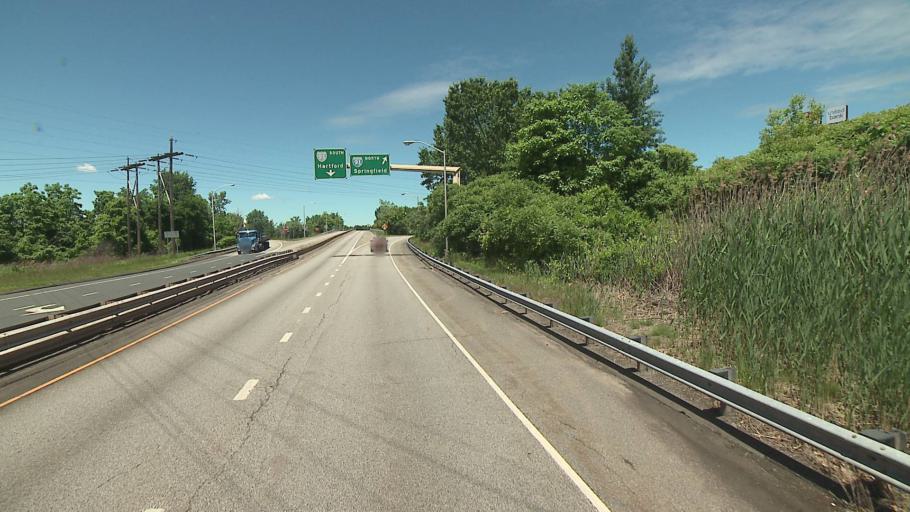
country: US
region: Connecticut
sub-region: Hartford County
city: Windsor Locks
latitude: 41.9182
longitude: -72.6118
